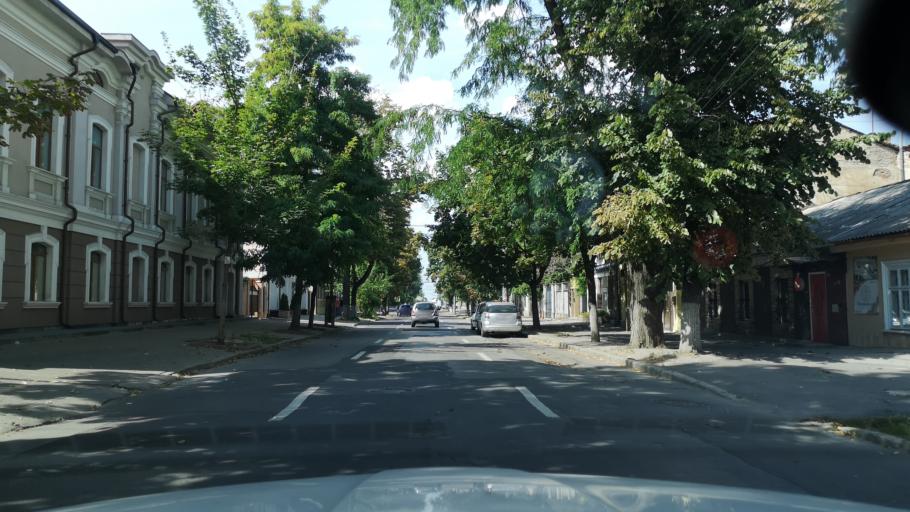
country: MD
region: Chisinau
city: Chisinau
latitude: 47.0246
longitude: 28.8208
